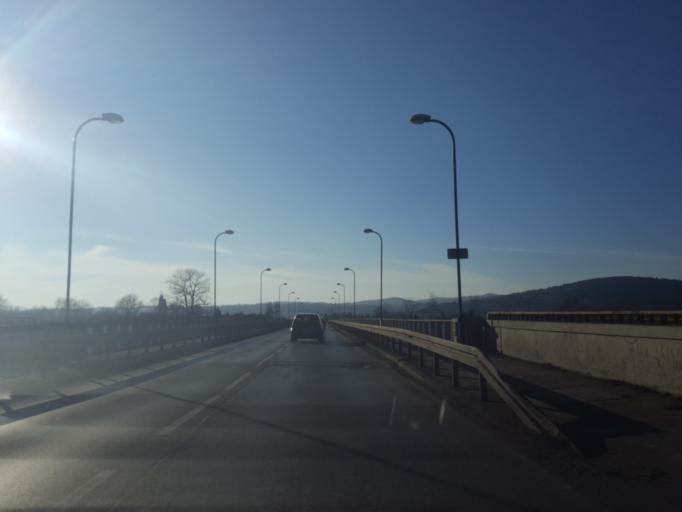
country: PL
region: Lesser Poland Voivodeship
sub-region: Powiat nowosadecki
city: Nowy Sacz
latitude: 49.6296
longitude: 20.6886
